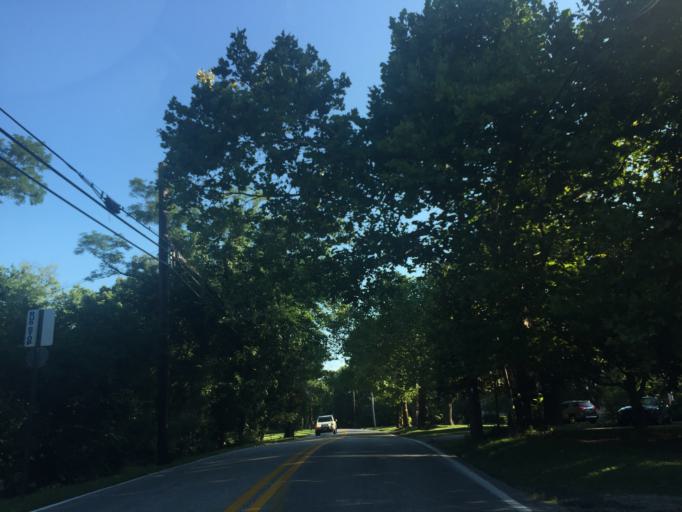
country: US
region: Maryland
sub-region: Baltimore County
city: Catonsville
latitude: 39.2766
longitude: -76.7552
